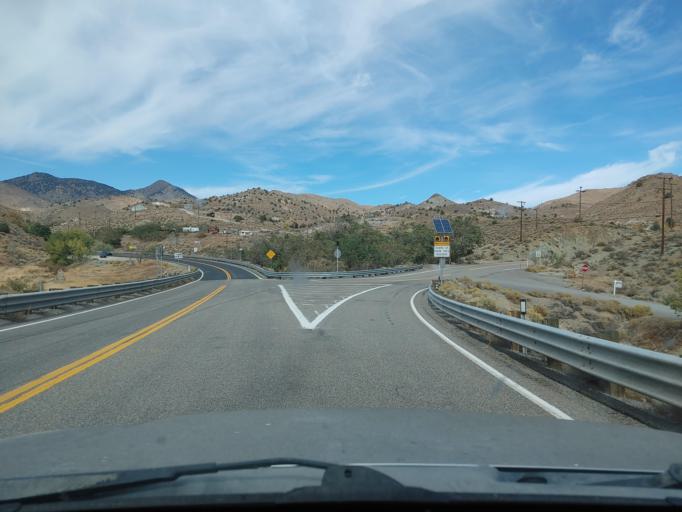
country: US
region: Nevada
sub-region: Lyon County
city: Dayton
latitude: 39.2574
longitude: -119.6358
